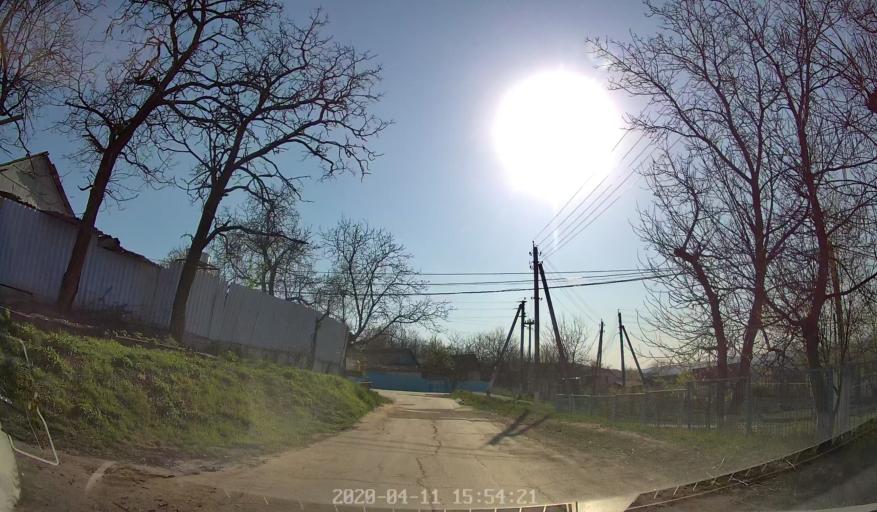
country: MD
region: Chisinau
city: Vadul lui Voda
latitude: 47.0987
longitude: 29.1763
